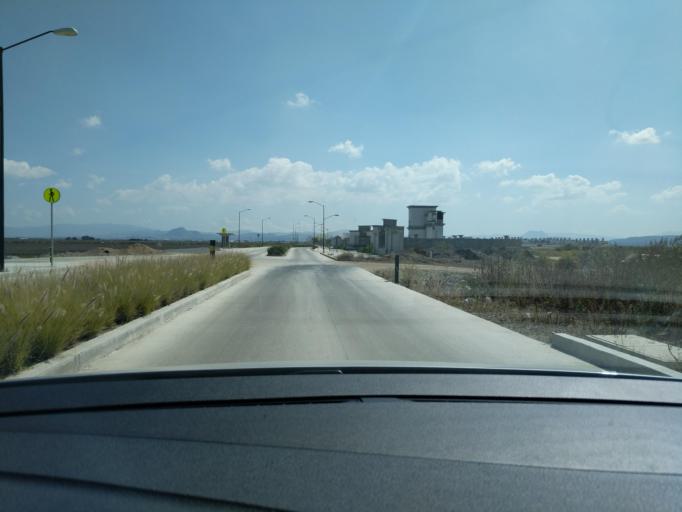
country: MX
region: Hidalgo
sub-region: Zempoala
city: Lindavista
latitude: 20.0066
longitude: -98.7784
